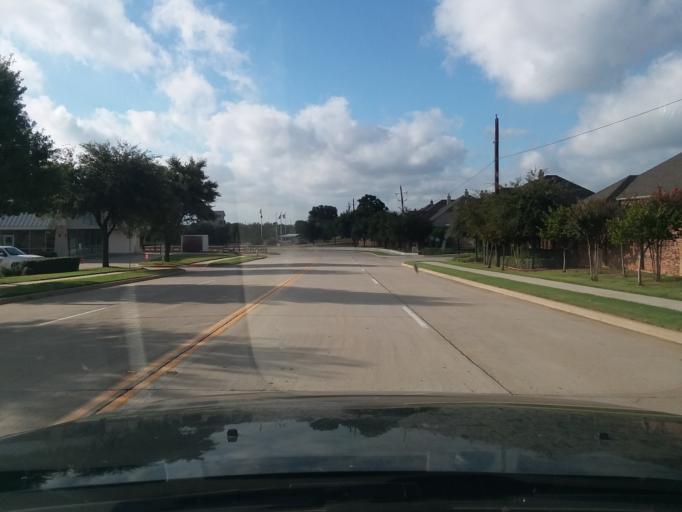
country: US
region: Texas
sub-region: Denton County
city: Hickory Creek
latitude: 33.1261
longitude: -97.0473
